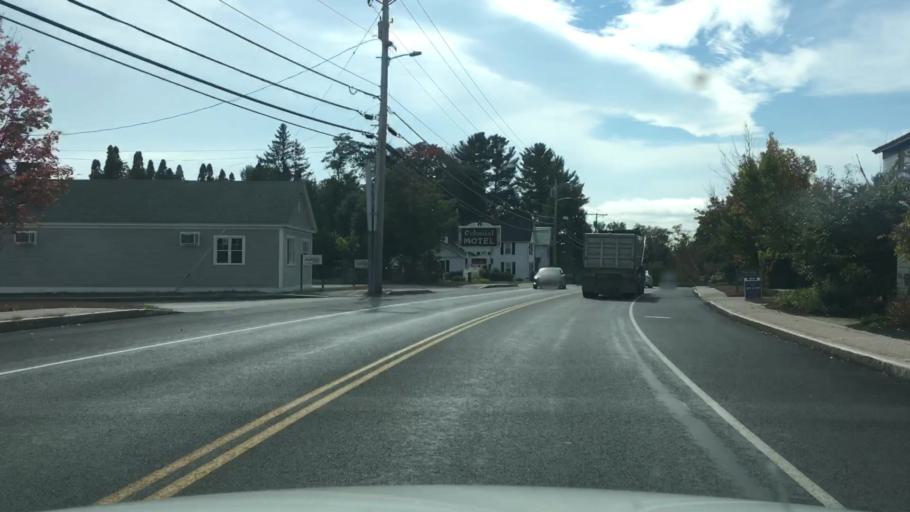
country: US
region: New Hampshire
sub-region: Carroll County
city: North Conway
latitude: 44.0469
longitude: -71.1243
